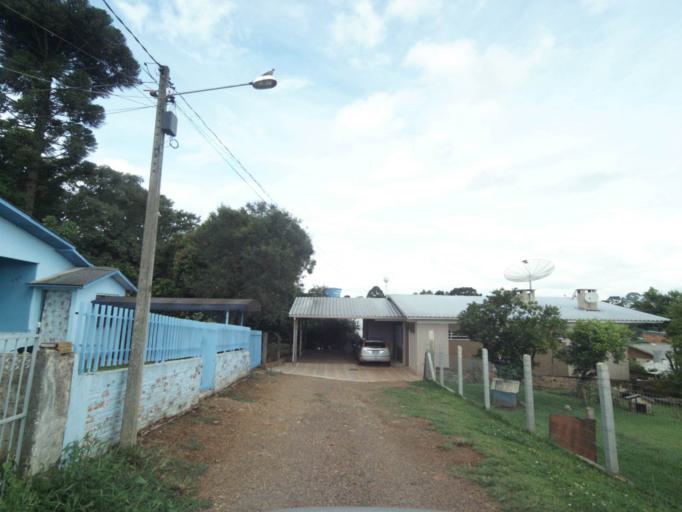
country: BR
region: Rio Grande do Sul
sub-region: Lagoa Vermelha
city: Lagoa Vermelha
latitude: -28.2099
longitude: -51.5365
